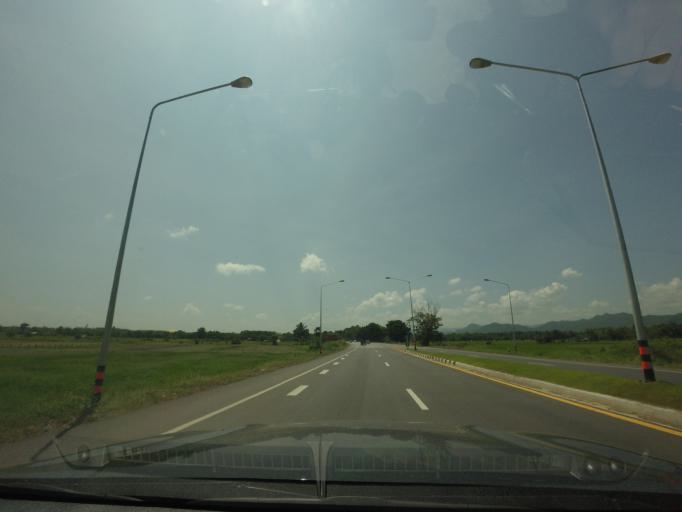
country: TH
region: Phetchabun
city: Lom Sak
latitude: 16.7584
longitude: 101.1811
